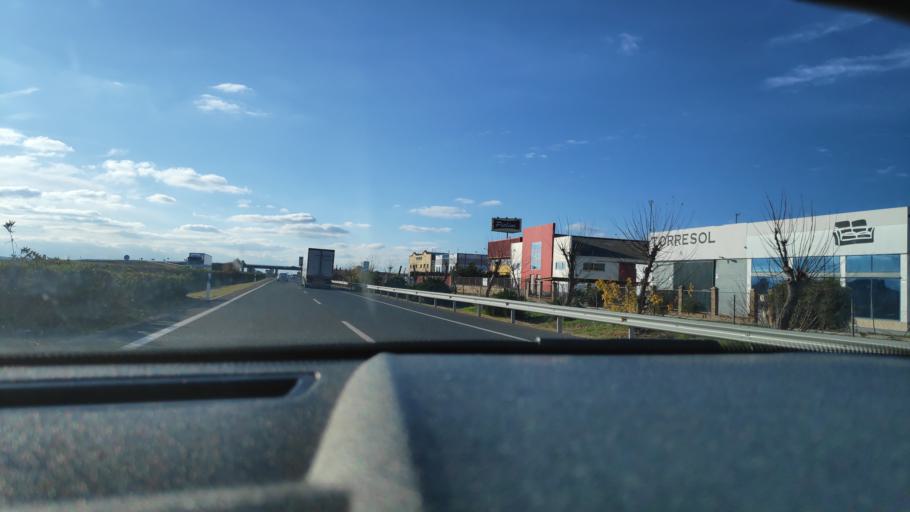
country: ES
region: Andalusia
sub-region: Provincia de Sevilla
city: Ecija
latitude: 37.5247
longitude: -5.1269
